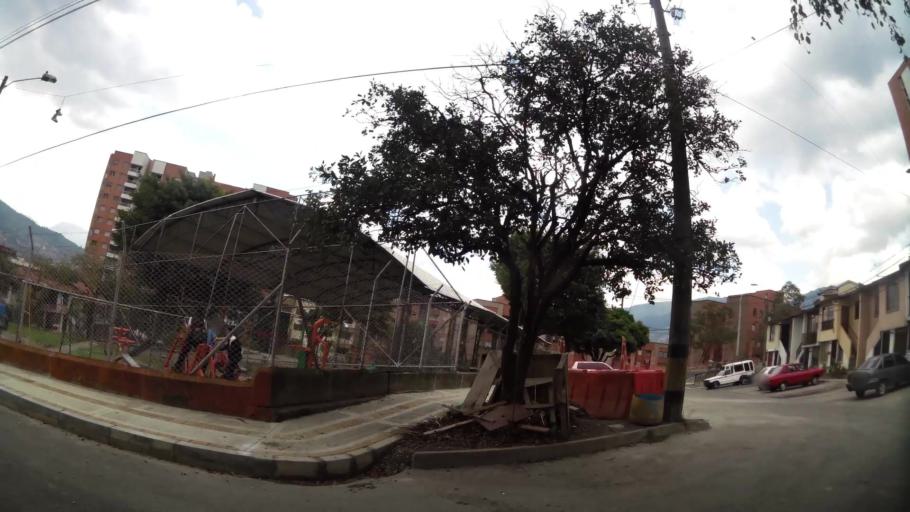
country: CO
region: Antioquia
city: Envigado
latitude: 6.1611
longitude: -75.5915
